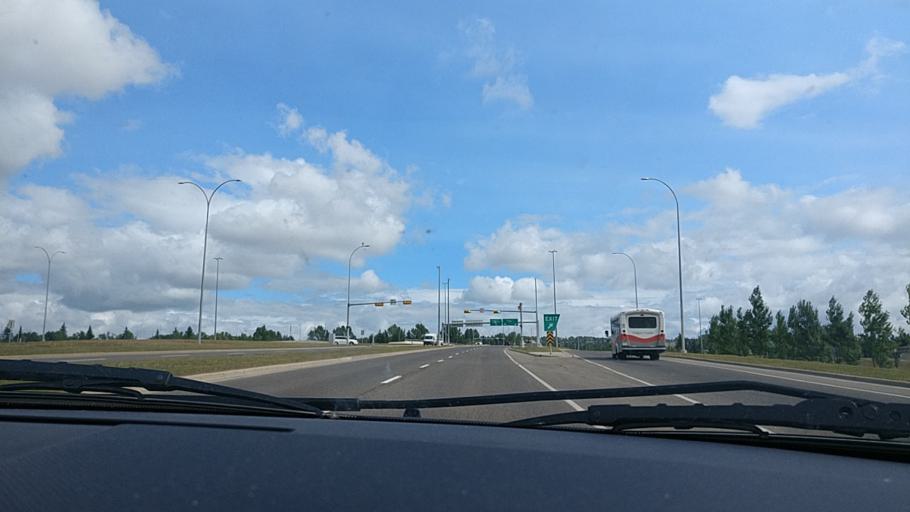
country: CA
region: Alberta
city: Calgary
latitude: 51.1085
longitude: -114.1796
